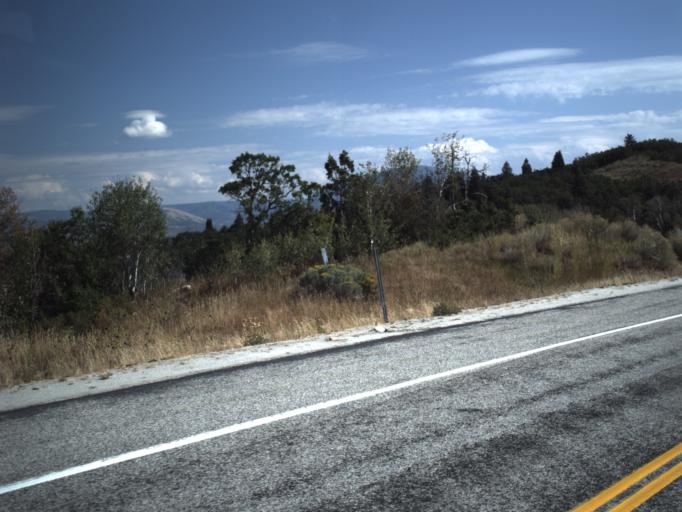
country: US
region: Utah
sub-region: Morgan County
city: Mountain Green
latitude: 41.2060
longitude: -111.8351
